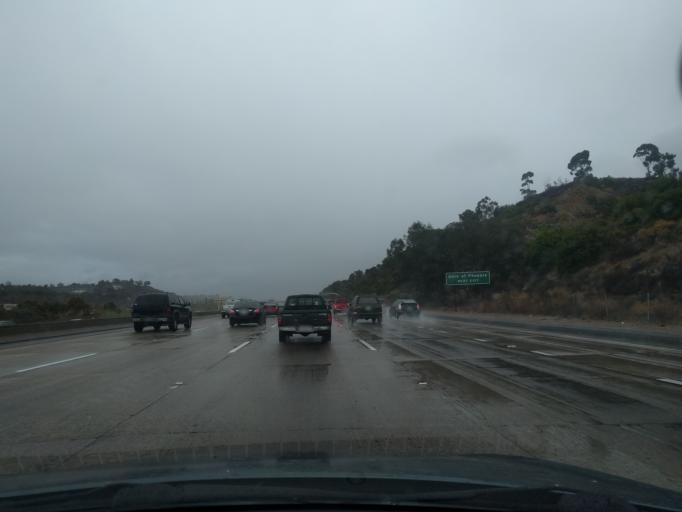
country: US
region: California
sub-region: San Diego County
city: La Mesa
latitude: 32.7996
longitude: -117.1123
